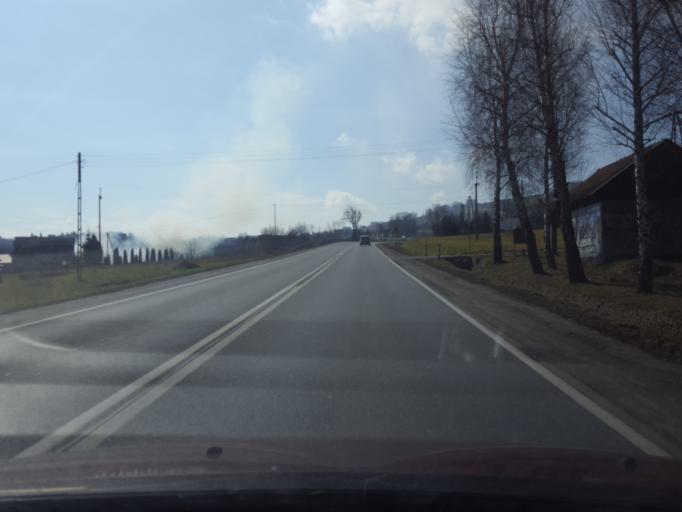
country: PL
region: Lesser Poland Voivodeship
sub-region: Powiat nowosadecki
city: Lososina Dolna
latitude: 49.7361
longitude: 20.6378
